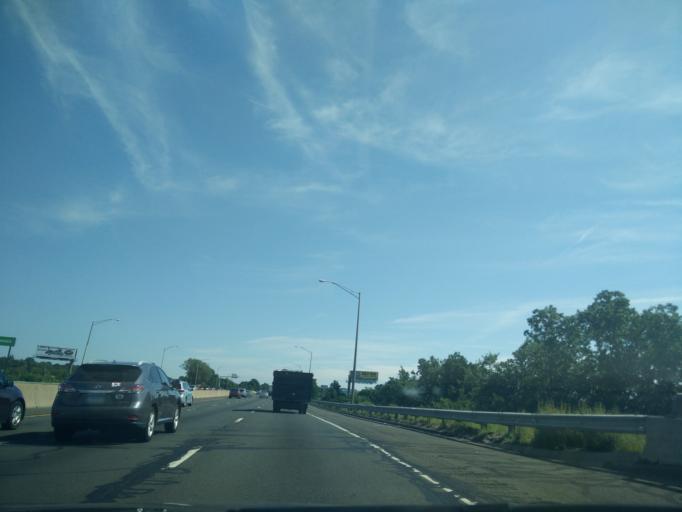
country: US
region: Connecticut
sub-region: Fairfield County
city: Stratford
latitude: 41.1766
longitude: -73.1500
